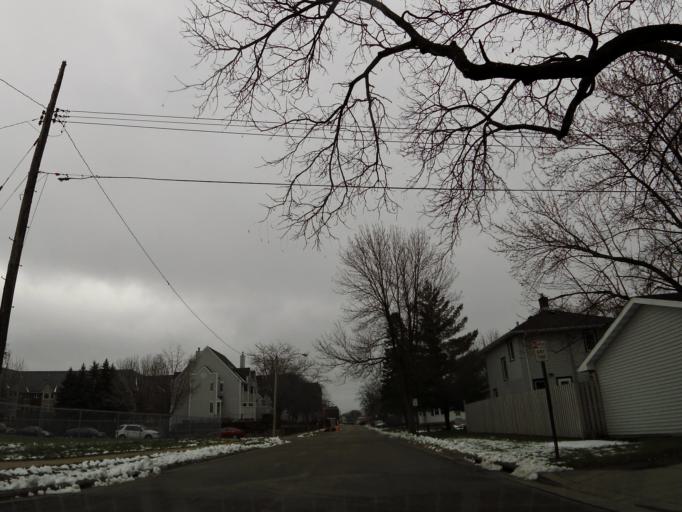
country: US
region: Minnesota
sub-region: Hennepin County
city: Minnetonka Mills
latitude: 44.9225
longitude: -93.4162
